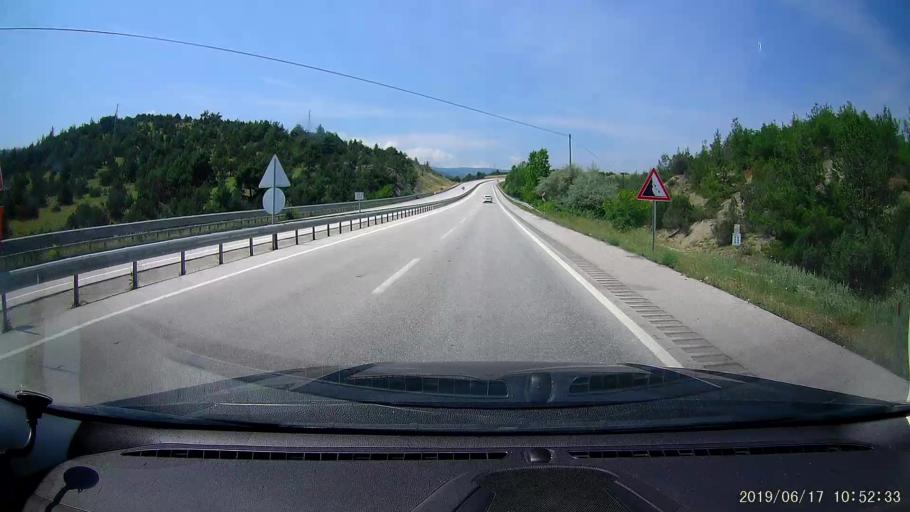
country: TR
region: Corum
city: Hacihamza
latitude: 41.0875
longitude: 34.3405
